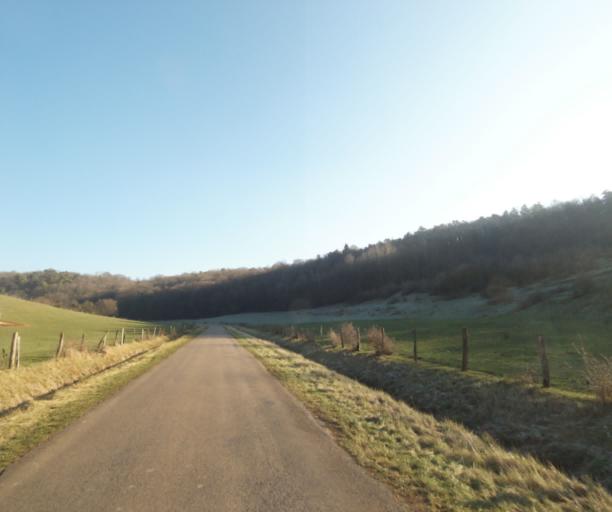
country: FR
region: Champagne-Ardenne
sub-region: Departement de la Haute-Marne
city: Chevillon
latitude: 48.5397
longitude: 5.1117
